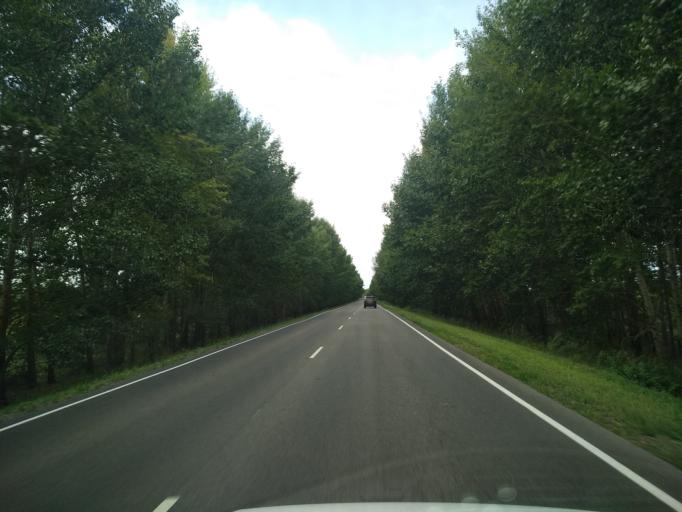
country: RU
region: Voronezj
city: Pereleshino
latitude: 51.8024
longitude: 40.1744
